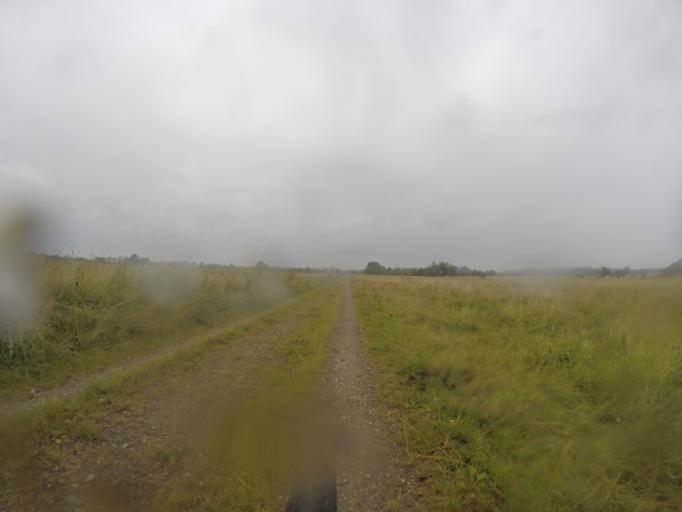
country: DK
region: Capital Region
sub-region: Hoje-Taastrup Kommune
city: Taastrup
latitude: 55.6910
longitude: 12.3117
